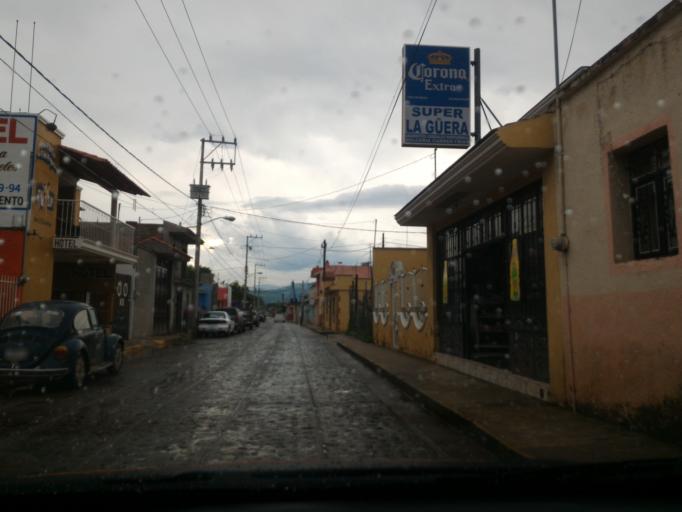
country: MX
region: Jalisco
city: San Andres Ixtlan
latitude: 19.8204
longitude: -103.4689
